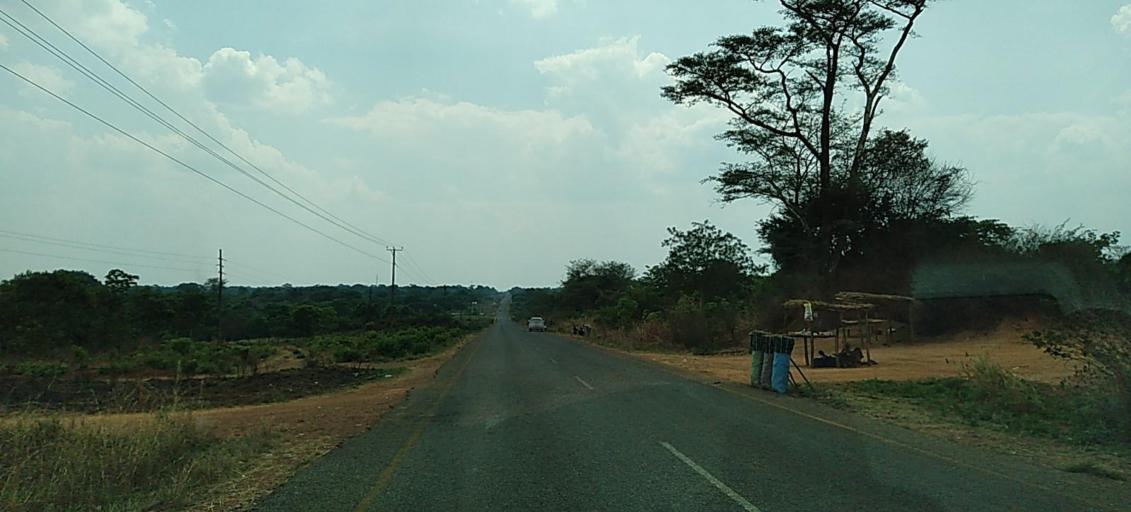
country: ZM
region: Copperbelt
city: Chingola
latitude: -12.8563
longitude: 27.6533
